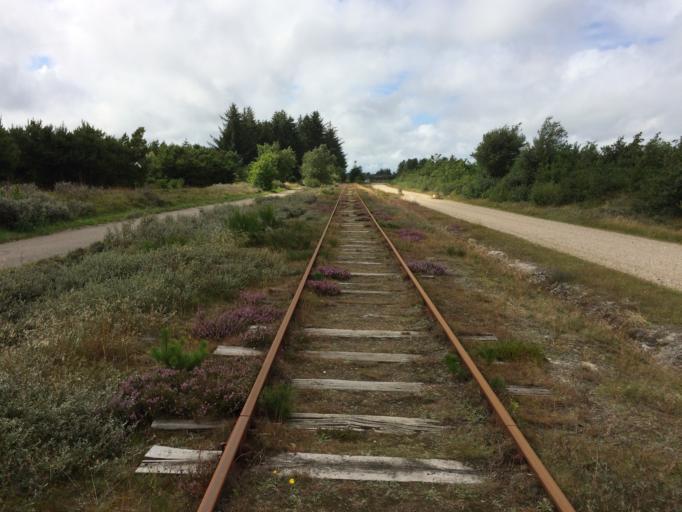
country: DK
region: South Denmark
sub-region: Varde Kommune
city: Oksbol
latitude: 55.7855
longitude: 8.2481
